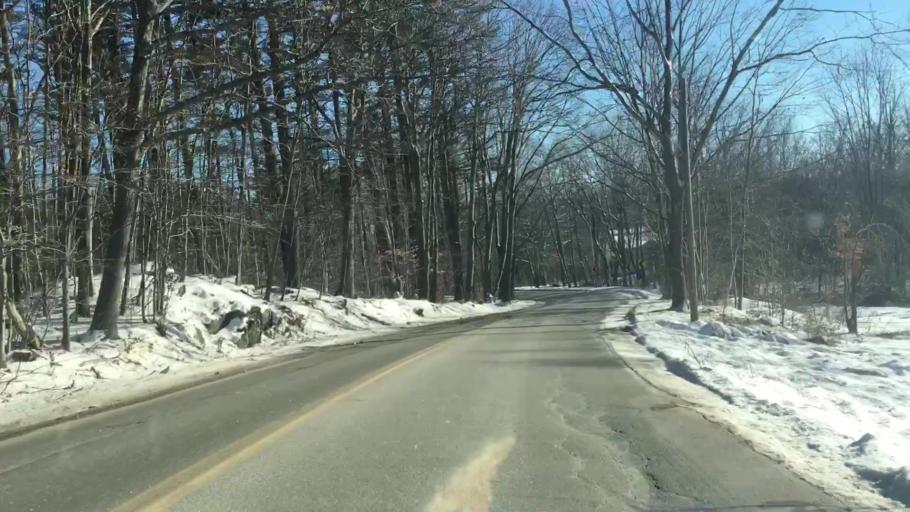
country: US
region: Maine
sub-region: Androscoggin County
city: Lewiston
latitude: 44.1077
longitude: -70.1801
